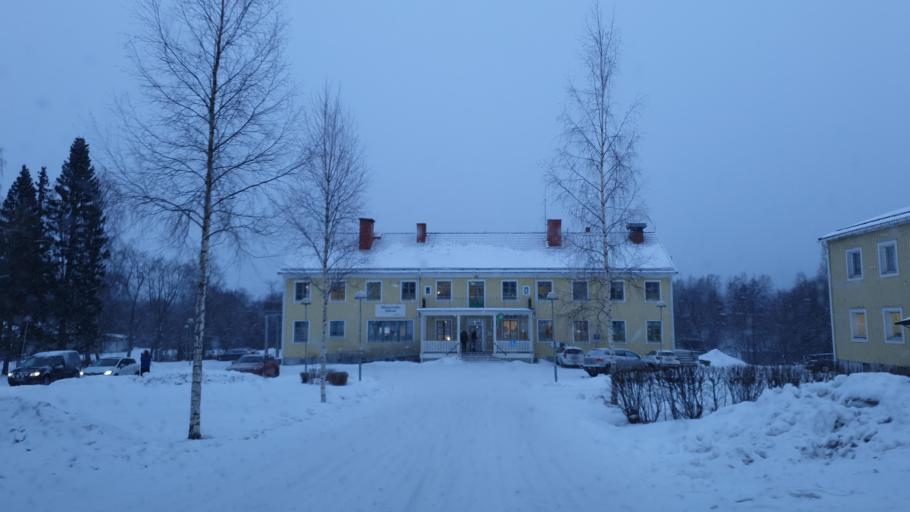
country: SE
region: Vaesternorrland
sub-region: OErnskoeldsviks Kommun
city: Ornskoldsvik
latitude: 63.2924
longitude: 18.6177
